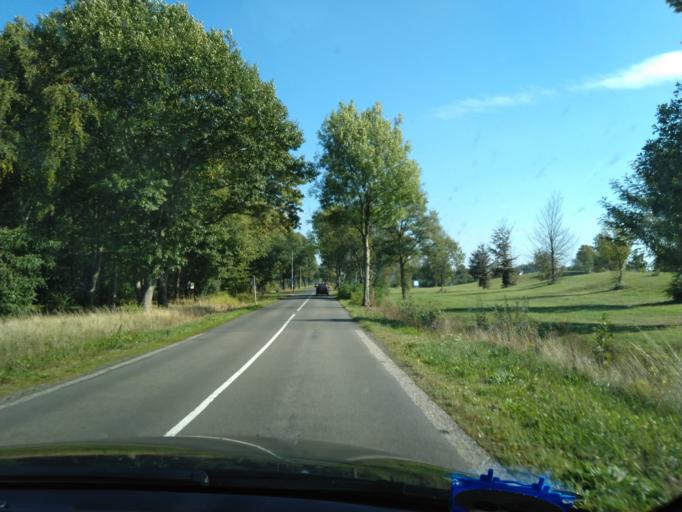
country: NL
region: Groningen
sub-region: Gemeente Veendam
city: Veendam
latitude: 53.0907
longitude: 6.8443
